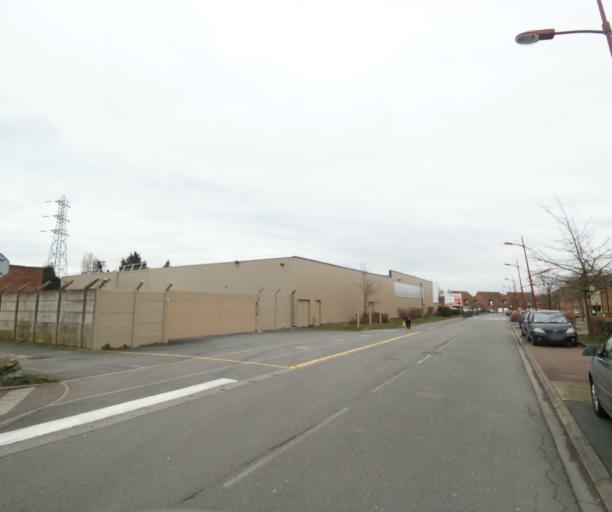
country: FR
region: Nord-Pas-de-Calais
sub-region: Departement du Nord
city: Beuvrages
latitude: 50.3838
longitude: 3.5055
